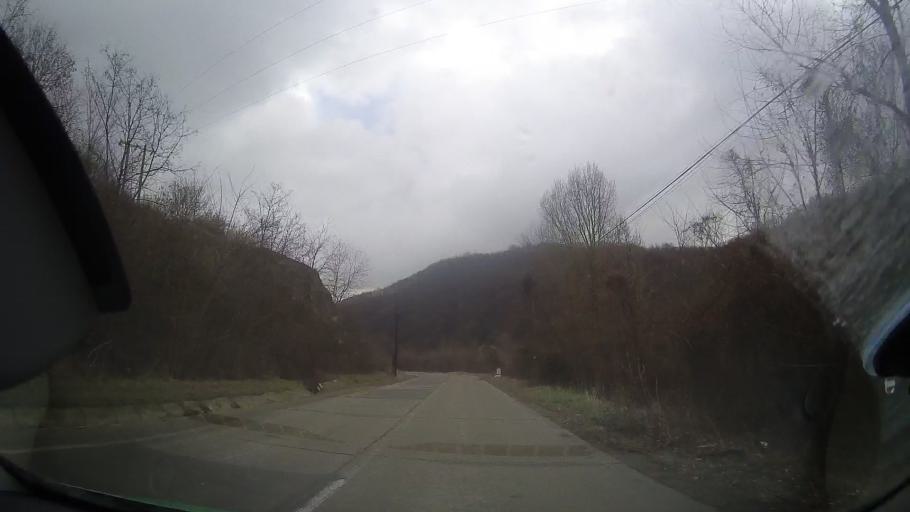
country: RO
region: Cluj
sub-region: Comuna Moldovenesti
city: Moldovenesti
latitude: 46.5068
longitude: 23.6498
